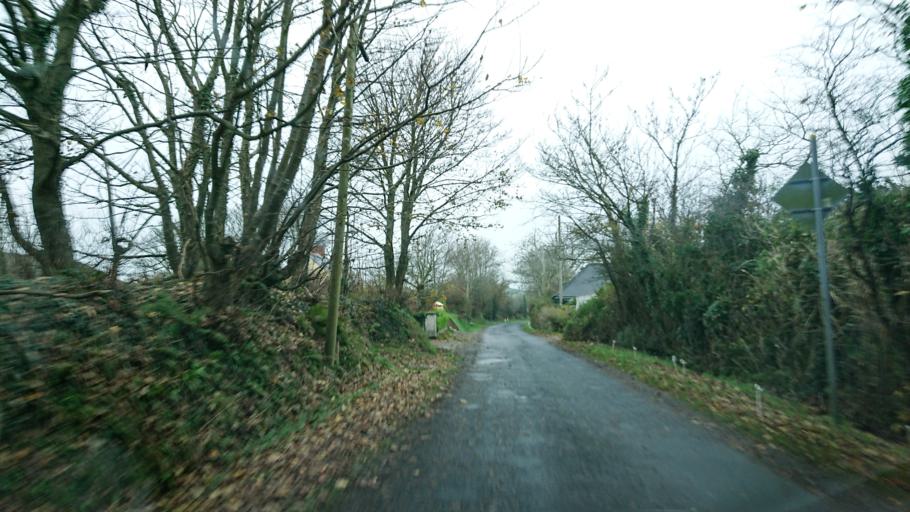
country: IE
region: Munster
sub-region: Waterford
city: Dunmore East
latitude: 52.1734
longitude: -7.0172
